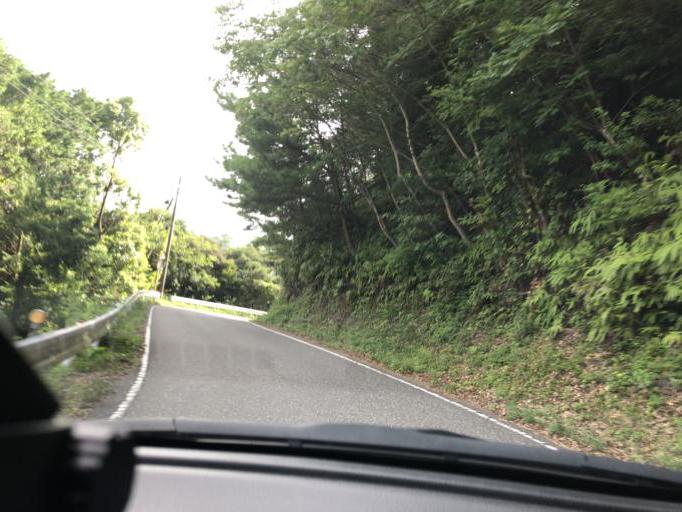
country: JP
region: Kochi
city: Kochi-shi
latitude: 33.5967
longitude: 133.5089
